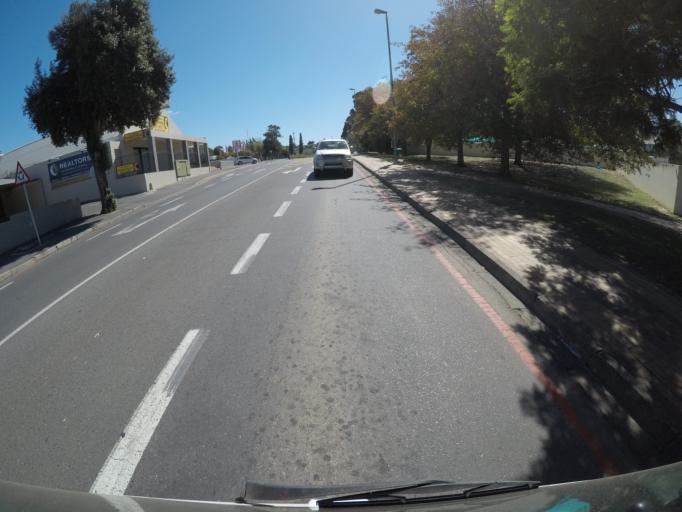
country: ZA
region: Western Cape
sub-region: City of Cape Town
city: Kraaifontein
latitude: -33.8310
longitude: 18.6453
